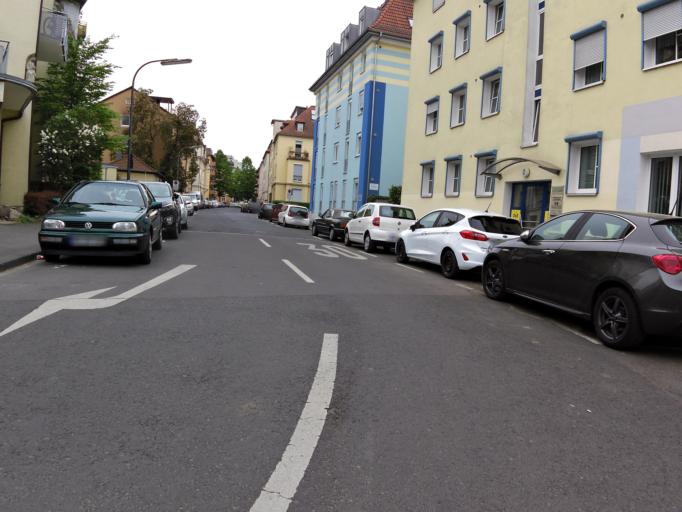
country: DE
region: Bavaria
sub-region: Regierungsbezirk Unterfranken
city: Wuerzburg
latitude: 49.7807
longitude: 9.9345
